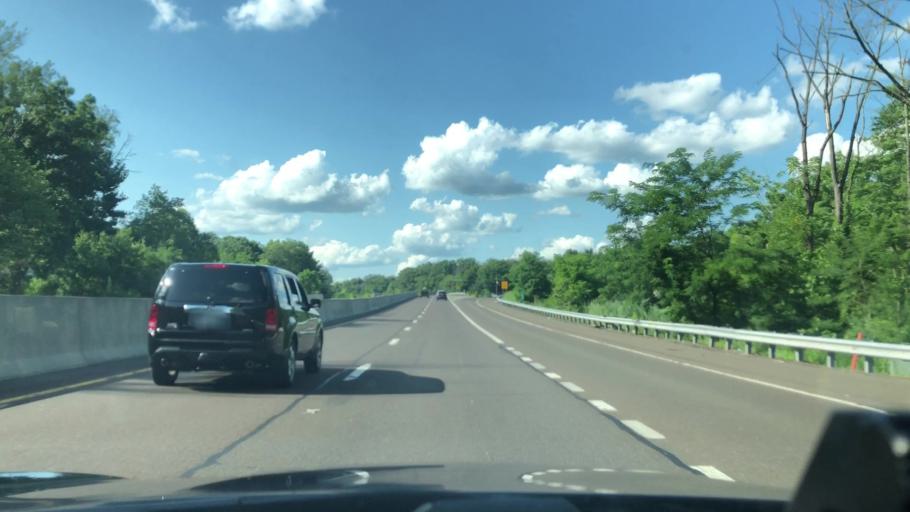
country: US
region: Pennsylvania
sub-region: Montgomery County
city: Fort Washington
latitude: 40.1584
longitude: -75.2011
